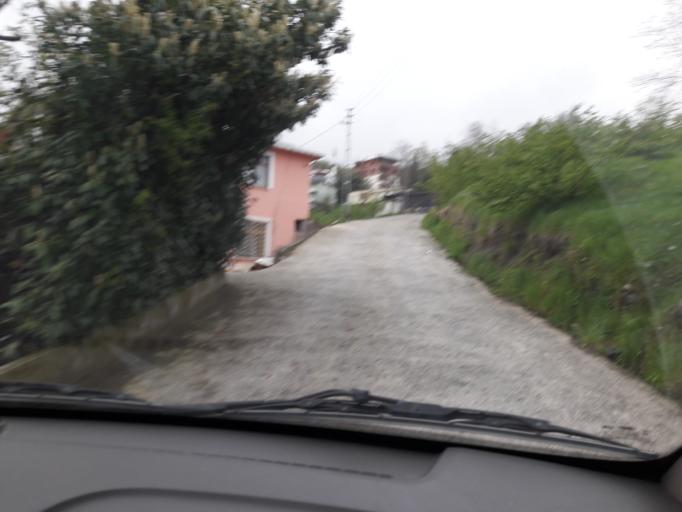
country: TR
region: Trabzon
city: Duzkoy
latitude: 40.9311
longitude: 39.4768
